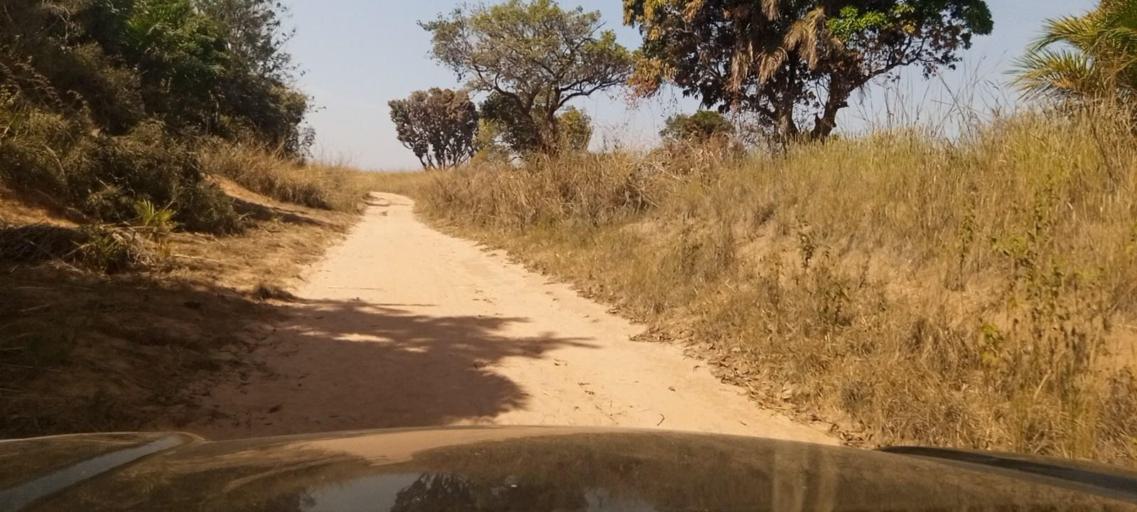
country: CD
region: Kasai-Oriental
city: Kabinda
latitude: -5.8034
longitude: 25.0277
